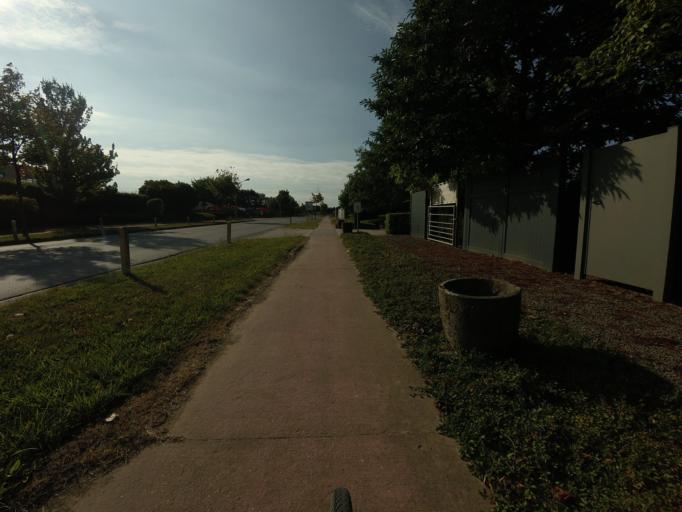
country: BE
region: Flanders
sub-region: Provincie Antwerpen
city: Ranst
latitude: 51.2081
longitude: 4.5852
